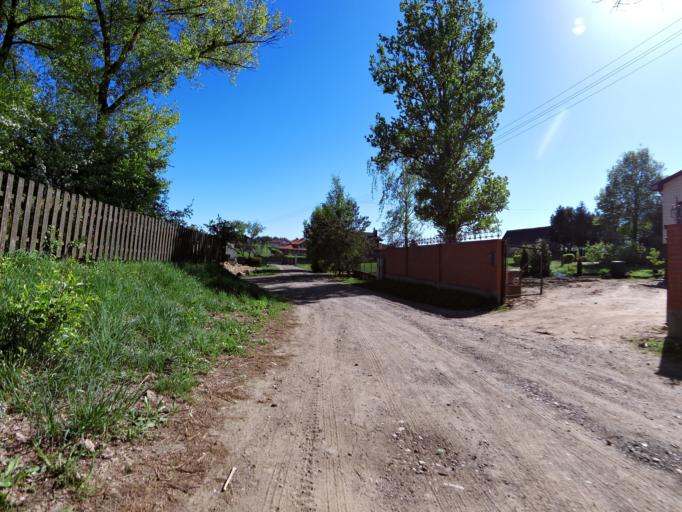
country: LT
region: Vilnius County
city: Pilaite
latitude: 54.6977
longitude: 25.1638
